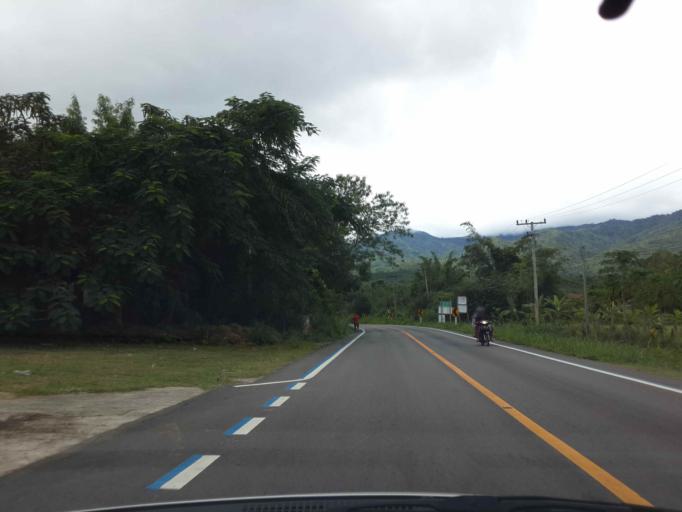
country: TH
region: Ratchaburi
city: Suan Phueng
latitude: 13.6034
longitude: 99.2312
